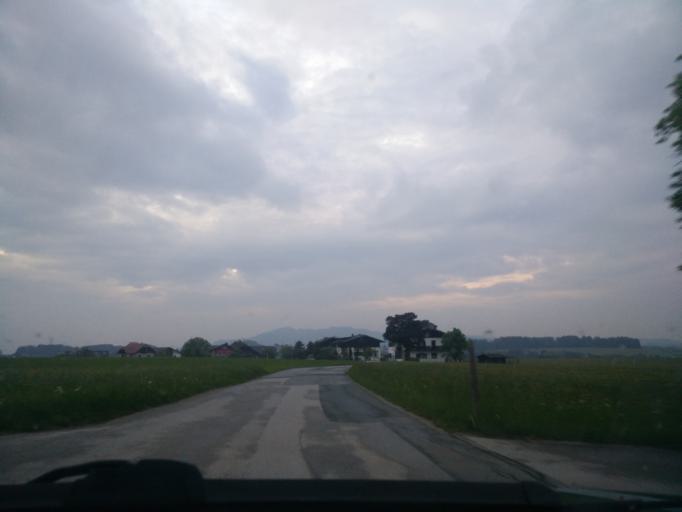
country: AT
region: Salzburg
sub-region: Politischer Bezirk Salzburg-Umgebung
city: Elixhausen
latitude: 47.8996
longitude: 13.0806
